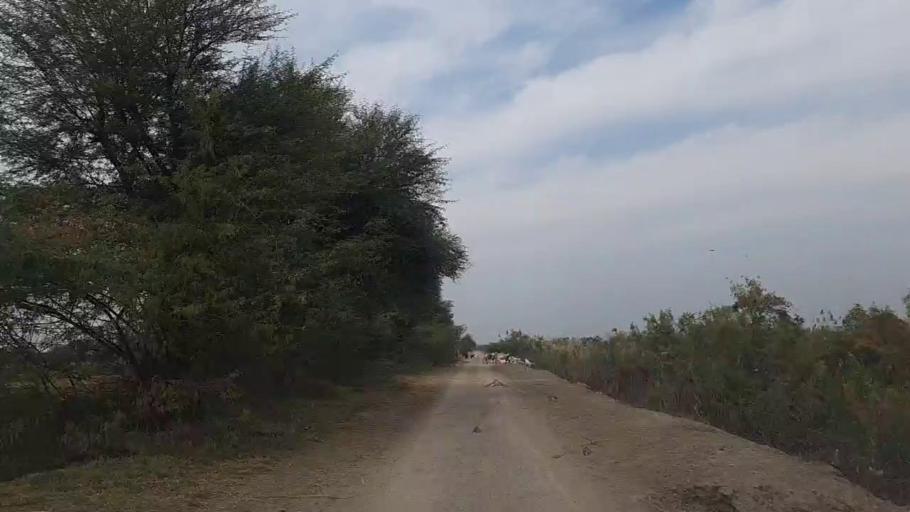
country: PK
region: Sindh
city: Daur
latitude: 26.4350
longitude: 68.4639
